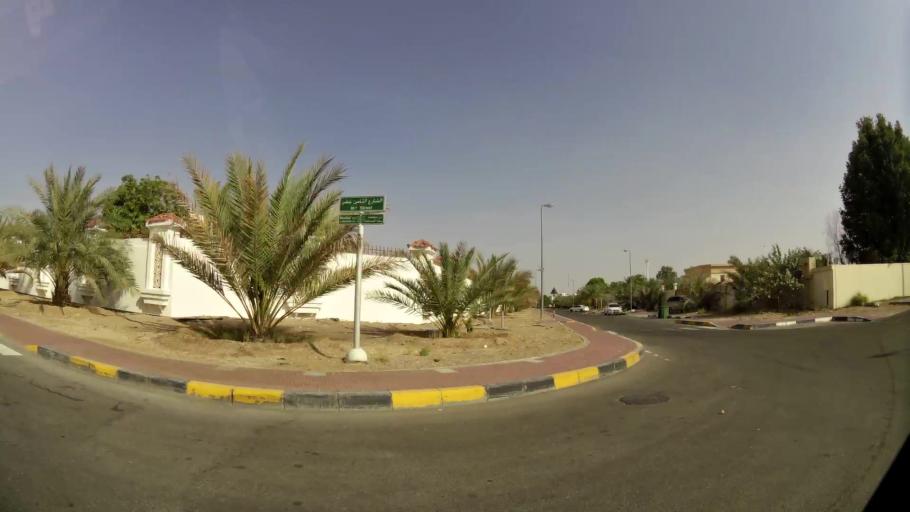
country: AE
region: Abu Dhabi
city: Al Ain
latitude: 24.2321
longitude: 55.6680
